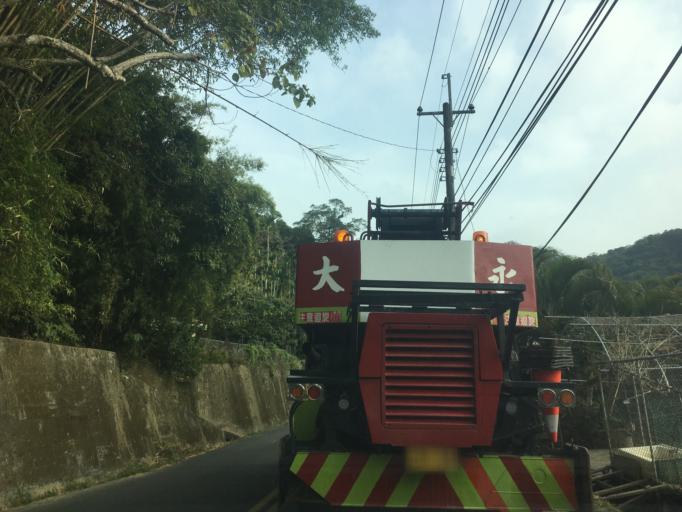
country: TW
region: Taiwan
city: Fengyuan
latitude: 24.2298
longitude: 120.7528
